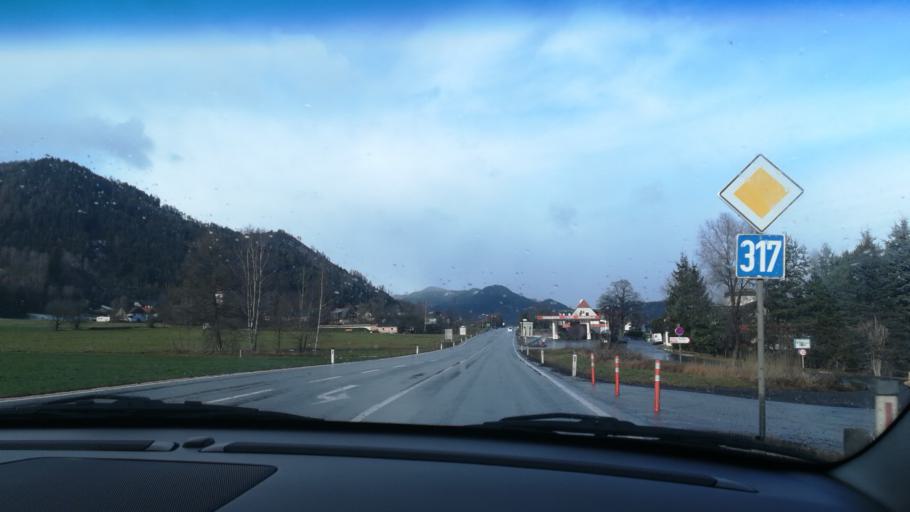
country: AT
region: Styria
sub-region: Politischer Bezirk Murtal
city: Sankt Peter ob Judenburg
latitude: 47.1832
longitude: 14.5974
